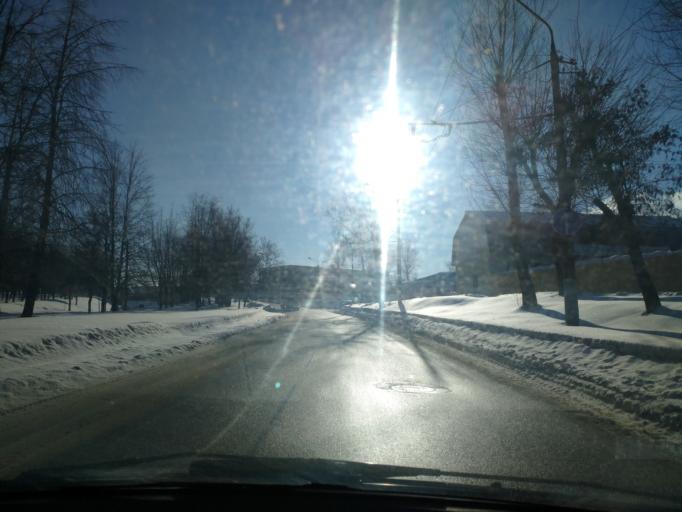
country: BY
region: Mogilev
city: Buynichy
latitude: 53.8938
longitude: 30.2979
